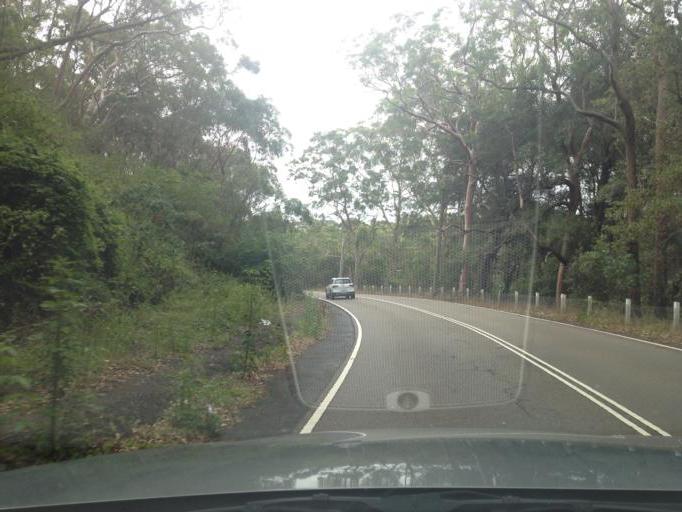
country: AU
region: New South Wales
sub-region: Ku-ring-gai
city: Lindfield
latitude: -33.7849
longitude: 151.1551
